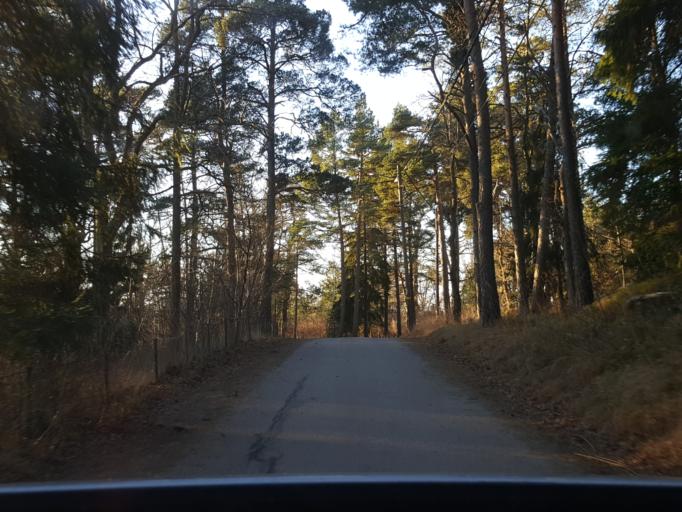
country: SE
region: Stockholm
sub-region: Nacka Kommun
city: Fisksatra
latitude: 59.3155
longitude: 18.2419
